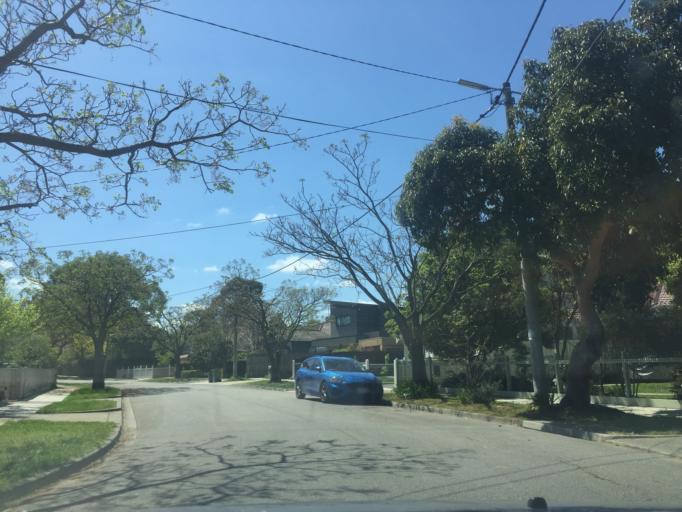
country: AU
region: Victoria
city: Ivanhoe East
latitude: -37.7694
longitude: 145.0515
